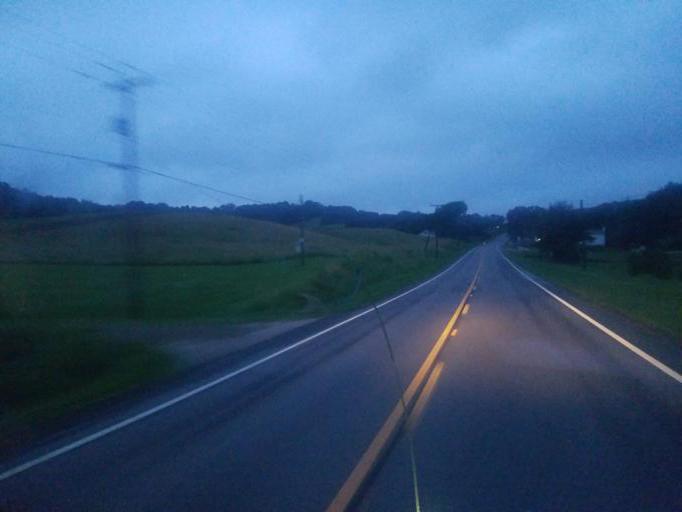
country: US
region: Ohio
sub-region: Carroll County
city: Carrollton
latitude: 40.5548
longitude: -81.0528
